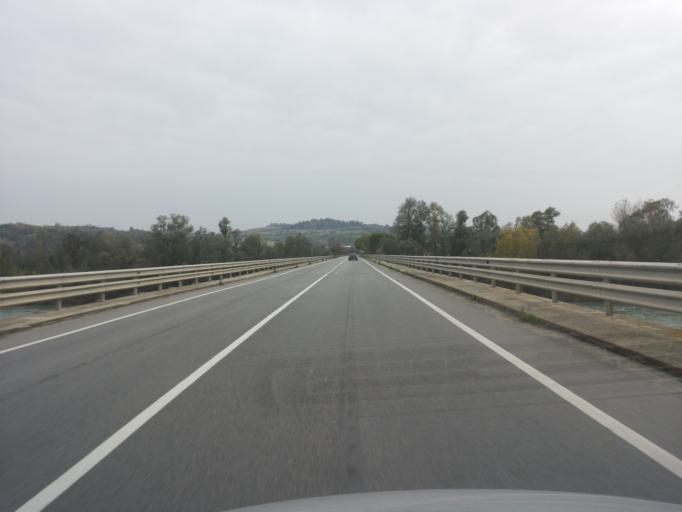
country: IT
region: Piedmont
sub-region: Provincia di Alessandria
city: Pontestura
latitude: 45.1477
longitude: 8.3400
